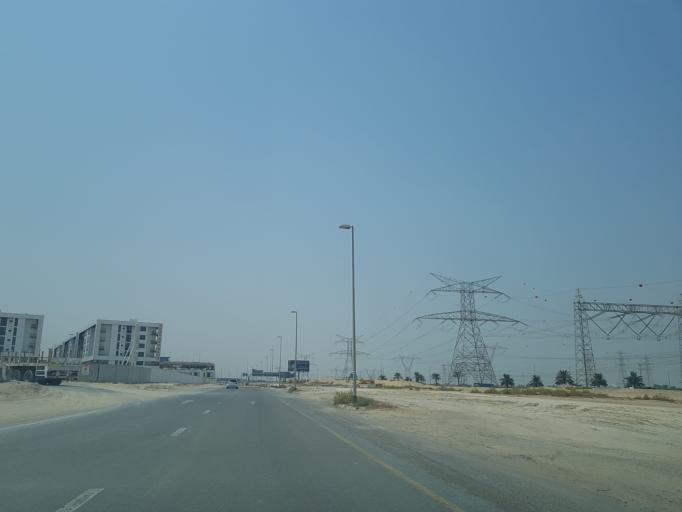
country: AE
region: Ash Shariqah
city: Sharjah
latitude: 25.2233
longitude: 55.4077
